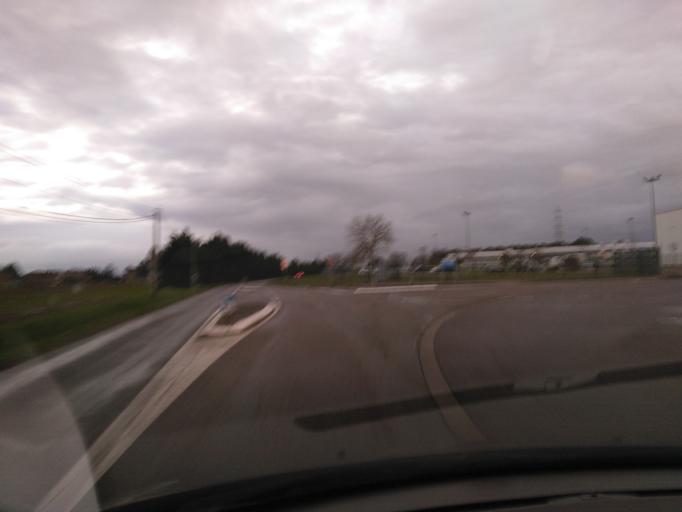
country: FR
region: Midi-Pyrenees
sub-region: Departement de la Haute-Garonne
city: Seilh
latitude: 43.6804
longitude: 1.3432
